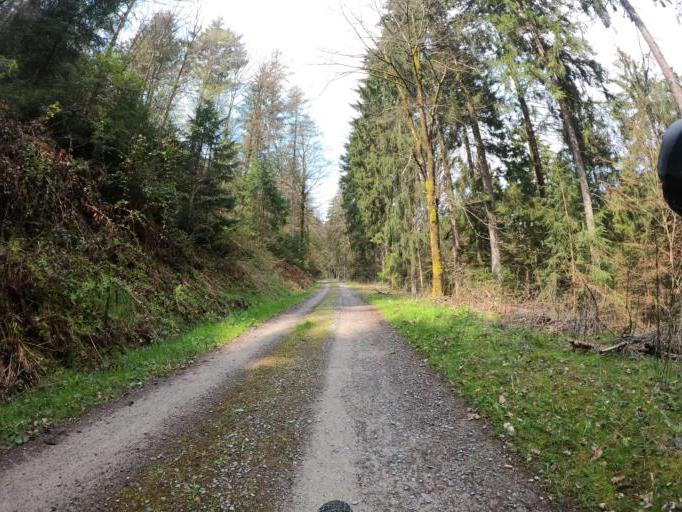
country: DE
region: Baden-Wuerttemberg
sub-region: Karlsruhe Region
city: Calw
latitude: 48.7365
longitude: 8.7156
